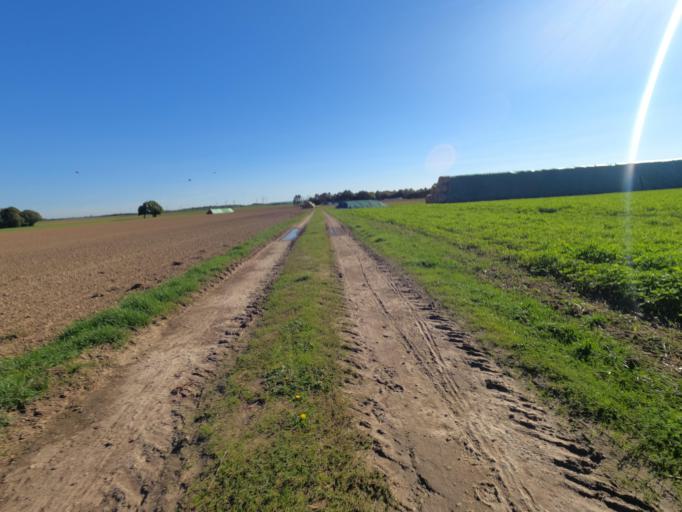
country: DE
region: North Rhine-Westphalia
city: Erkelenz
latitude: 51.0718
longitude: 6.3516
